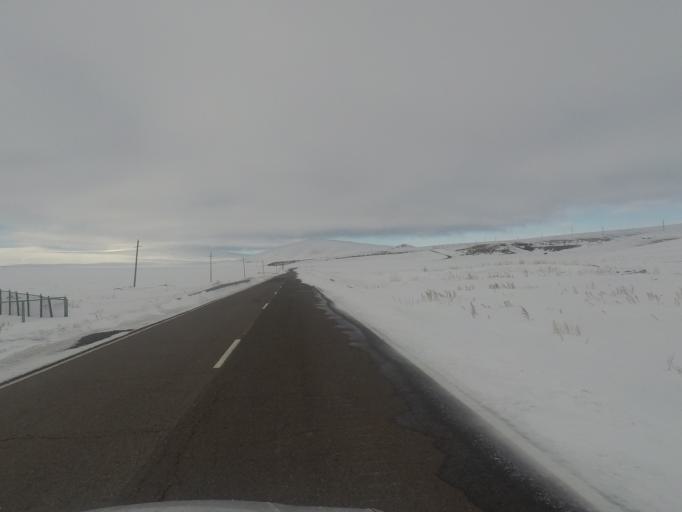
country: GE
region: Samtskhe-Javakheti
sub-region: Ninotsminda
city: Ninotsminda
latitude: 41.4286
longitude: 43.8369
